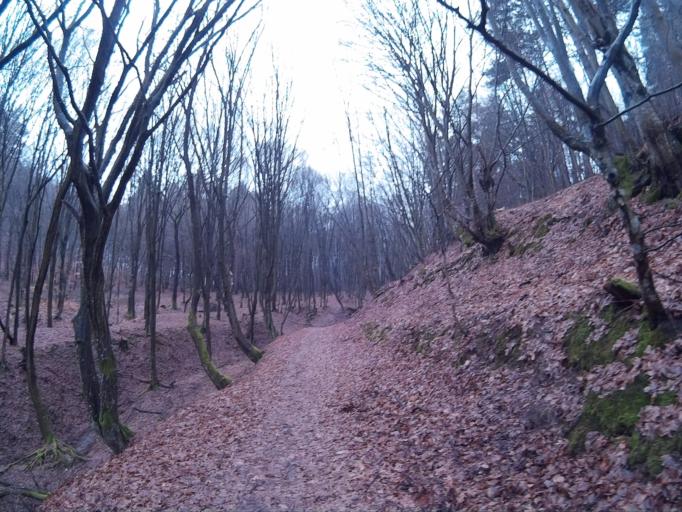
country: HU
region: Borsod-Abauj-Zemplen
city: Sarospatak
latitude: 48.4691
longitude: 21.4717
